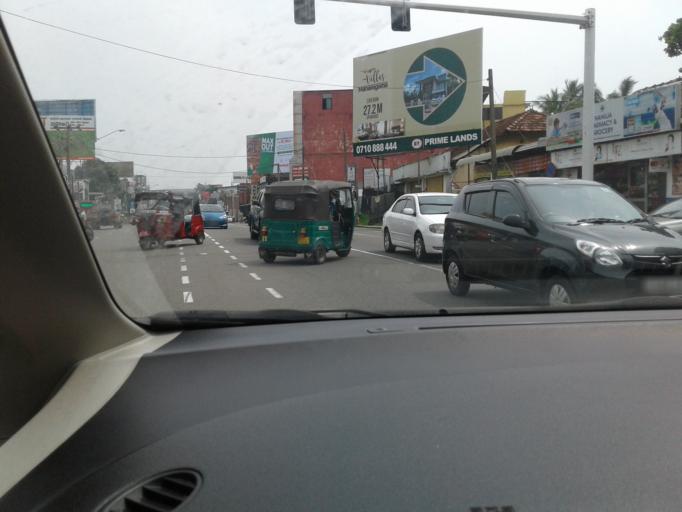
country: LK
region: Western
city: Maharagama
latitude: 6.8512
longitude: 79.9212
